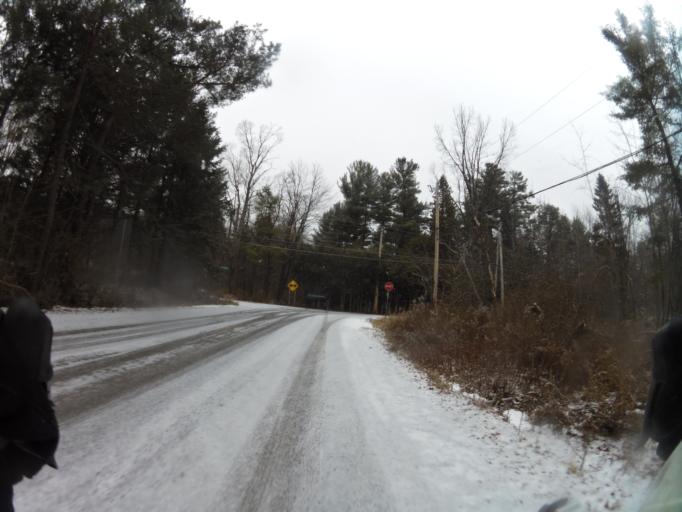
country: CA
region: Quebec
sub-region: Outaouais
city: Gatineau
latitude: 45.4905
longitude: -75.8410
